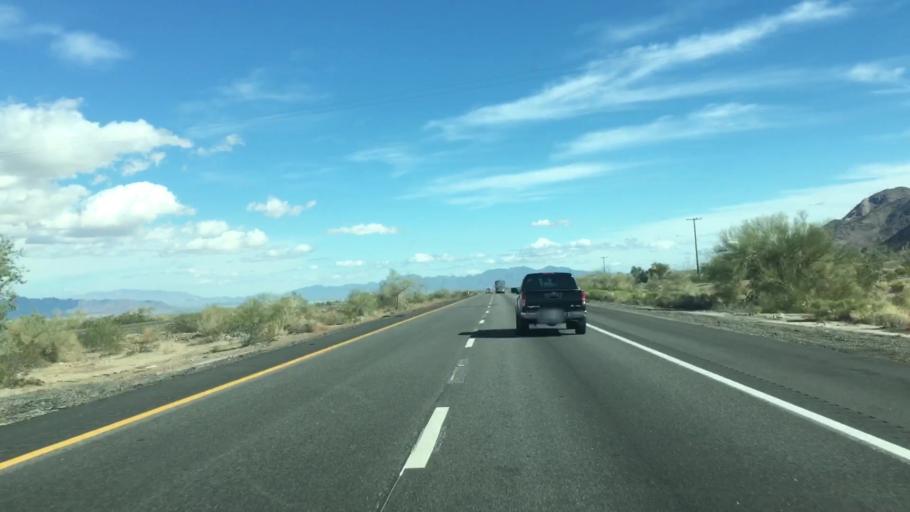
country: US
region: California
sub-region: Imperial County
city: Niland
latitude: 33.6877
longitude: -115.5179
